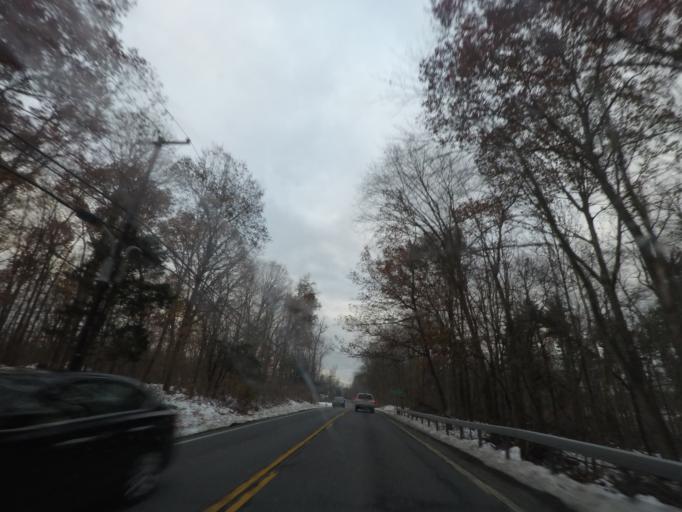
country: US
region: New York
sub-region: Orange County
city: Gardnertown
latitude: 41.5614
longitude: -74.0645
